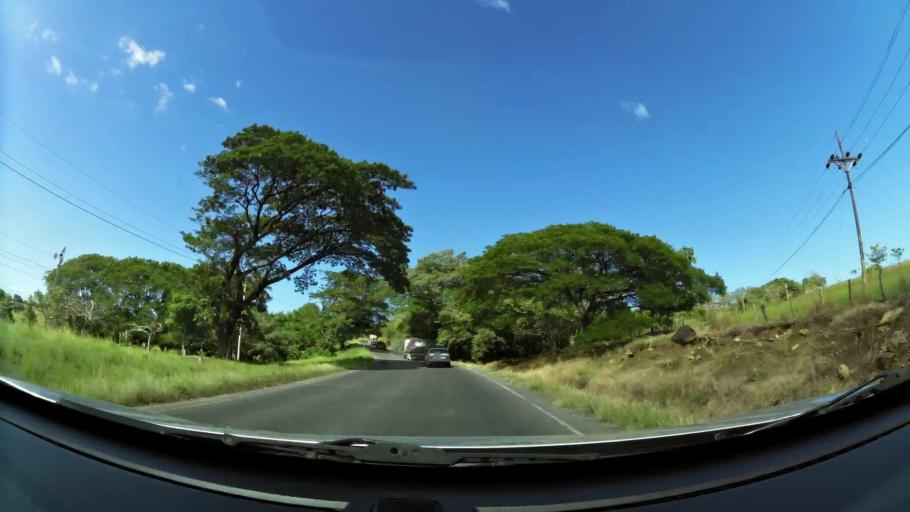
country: CR
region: Guanacaste
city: Juntas
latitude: 10.3230
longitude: -85.0480
